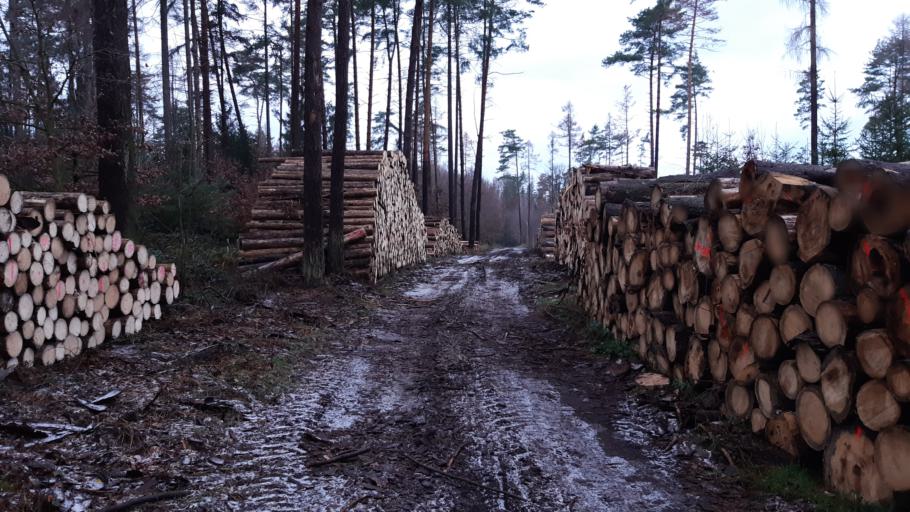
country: CZ
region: South Moravian
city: Drnovice
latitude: 49.2668
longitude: 16.9185
